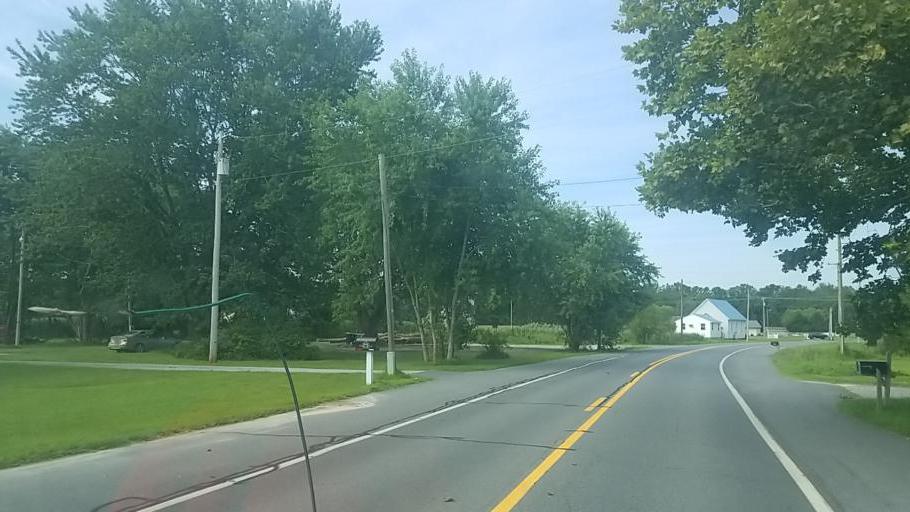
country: US
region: Delaware
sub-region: Sussex County
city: Selbyville
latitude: 38.5280
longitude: -75.1981
